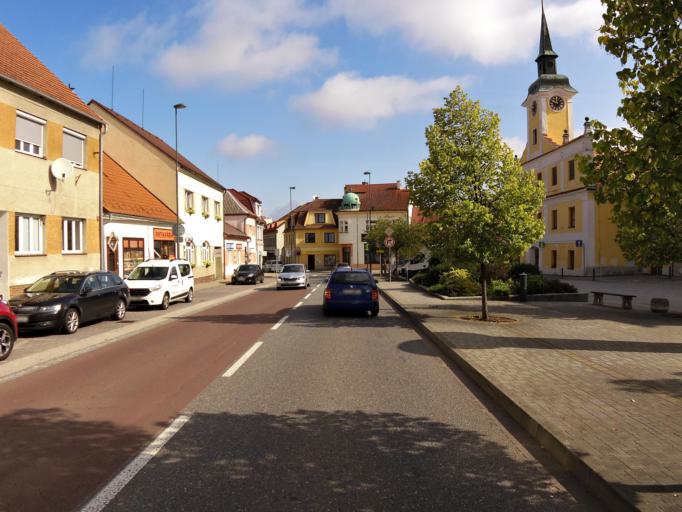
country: CZ
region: Jihocesky
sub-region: Okres Jindrichuv Hradec
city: Lomnice nad Luznici
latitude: 49.0818
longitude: 14.7181
